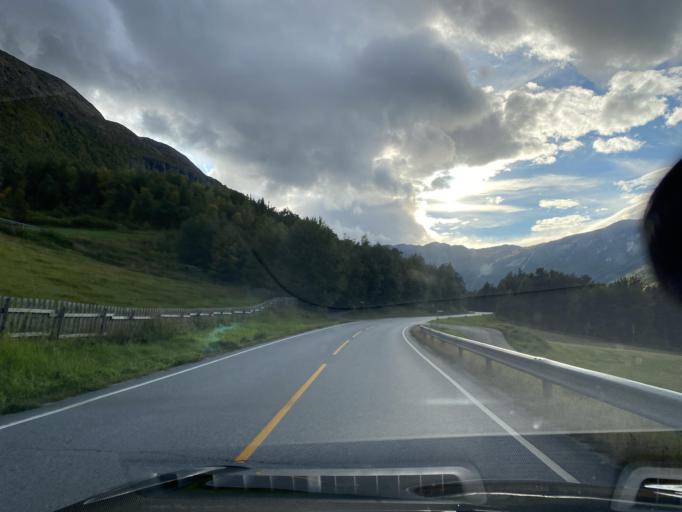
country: NO
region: Oppland
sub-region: Lom
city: Fossbergom
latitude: 61.8190
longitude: 8.5214
